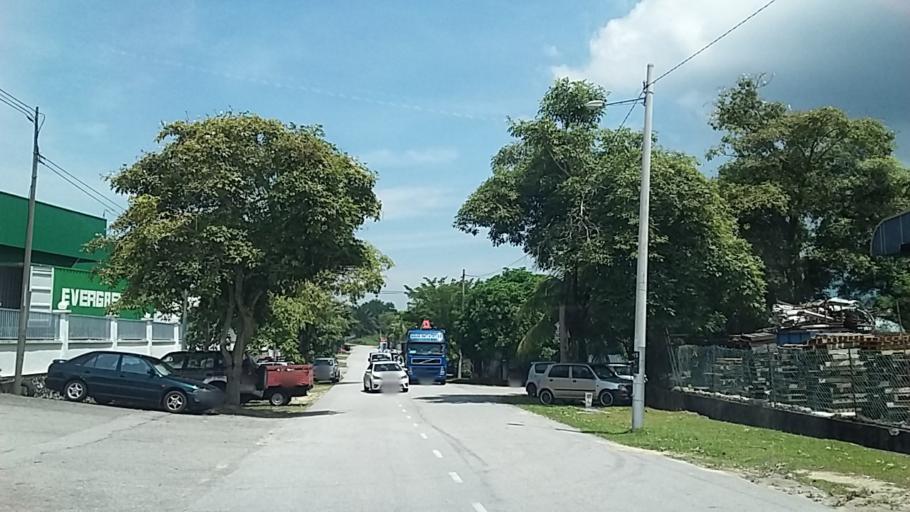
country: MY
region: Johor
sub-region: Daerah Batu Pahat
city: Batu Pahat
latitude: 1.7837
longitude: 102.9676
